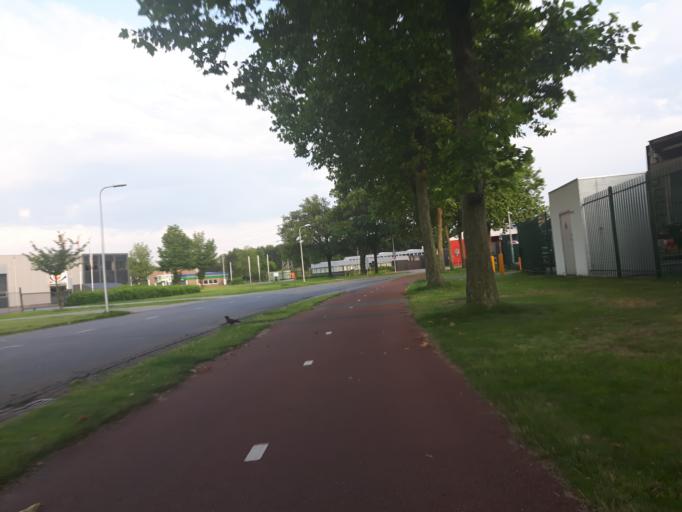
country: NL
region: Overijssel
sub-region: Gemeente Enschede
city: Enschede
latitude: 52.2203
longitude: 6.8503
